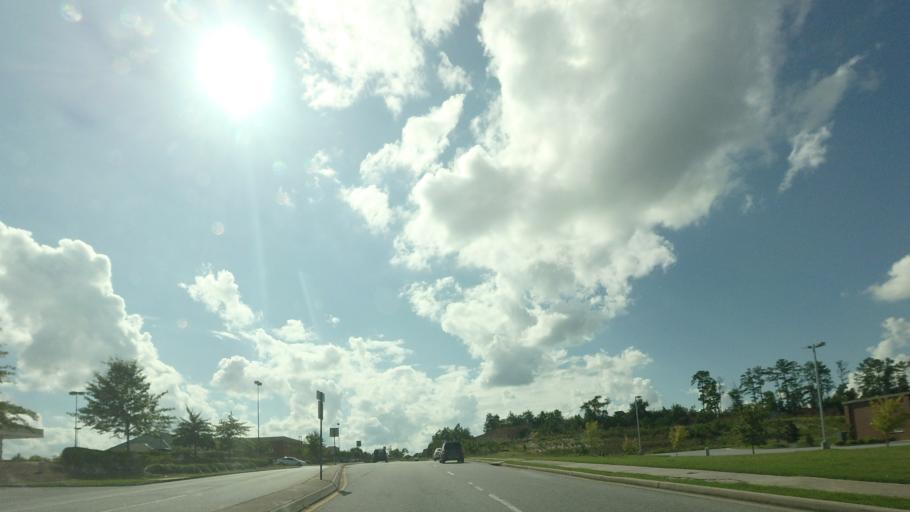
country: US
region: Georgia
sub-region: Bibb County
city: Macon
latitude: 32.8208
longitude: -83.7104
